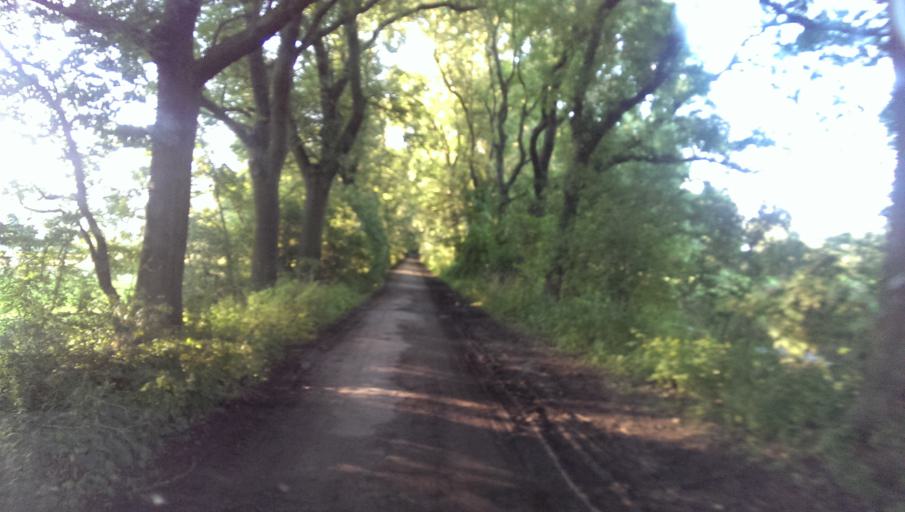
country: DE
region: Brandenburg
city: Trebbin
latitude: 52.2559
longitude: 13.1908
